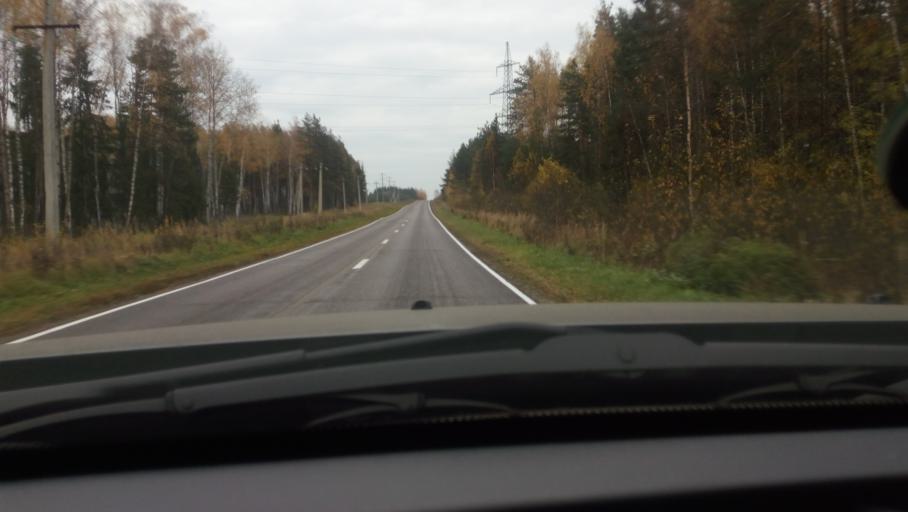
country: RU
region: Moskovskaya
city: Avsyunino
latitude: 55.5987
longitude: 39.2239
